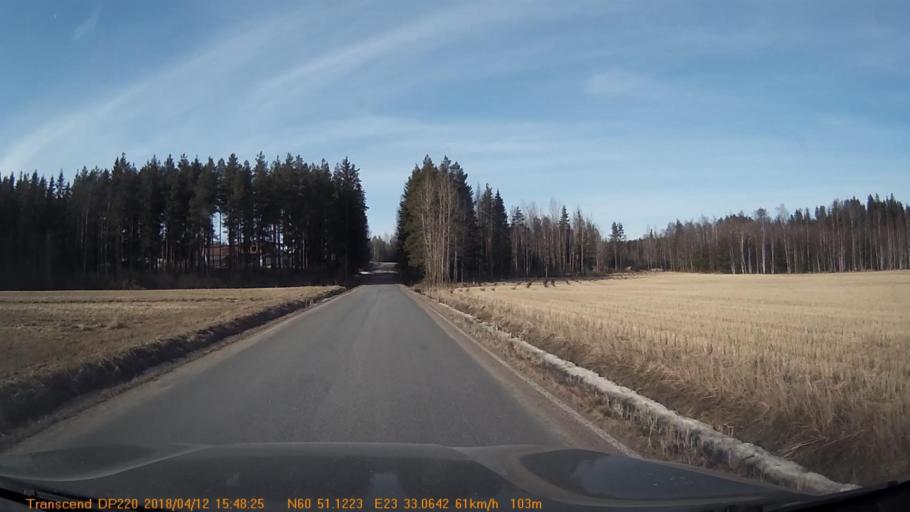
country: FI
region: Haeme
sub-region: Forssa
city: Forssa
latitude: 60.8523
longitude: 23.5509
